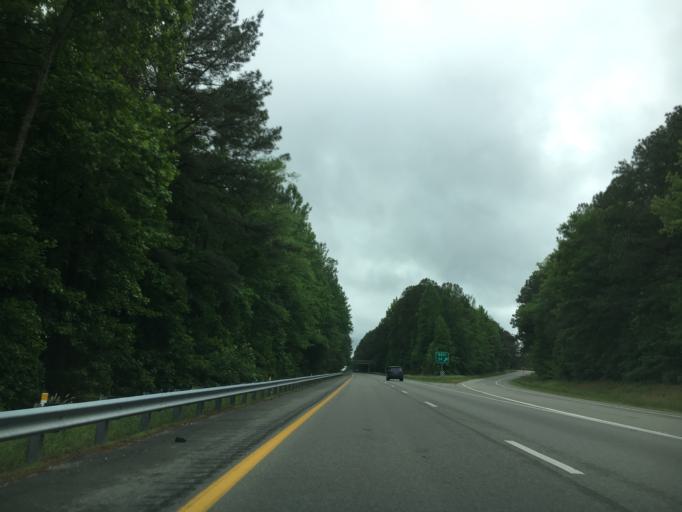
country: US
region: Virginia
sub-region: Brunswick County
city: Lawrenceville
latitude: 36.8974
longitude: -77.7996
